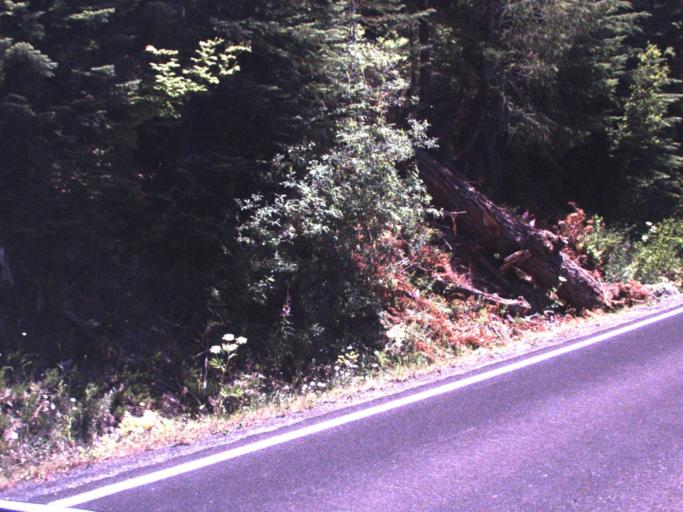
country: US
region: Washington
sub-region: King County
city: Enumclaw
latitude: 46.8424
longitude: -121.5305
